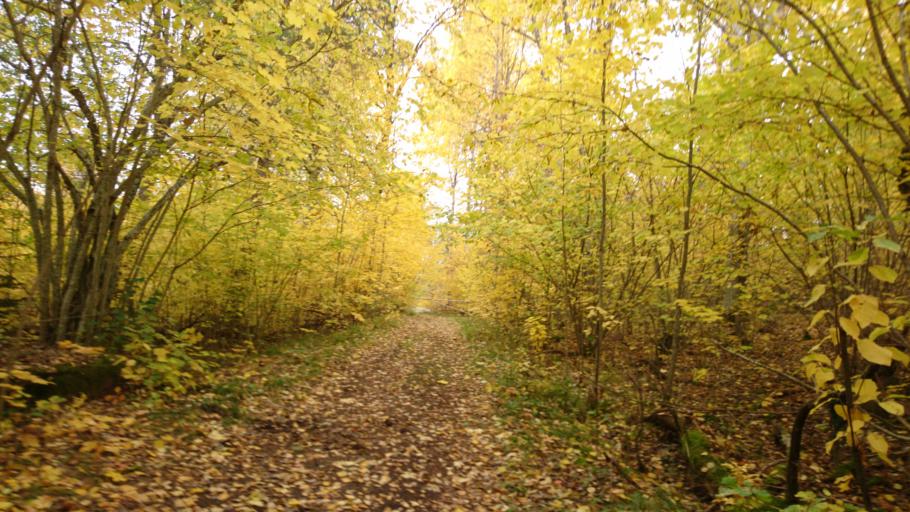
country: SE
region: Uppsala
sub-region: Knivsta Kommun
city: Knivsta
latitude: 59.8693
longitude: 17.9562
